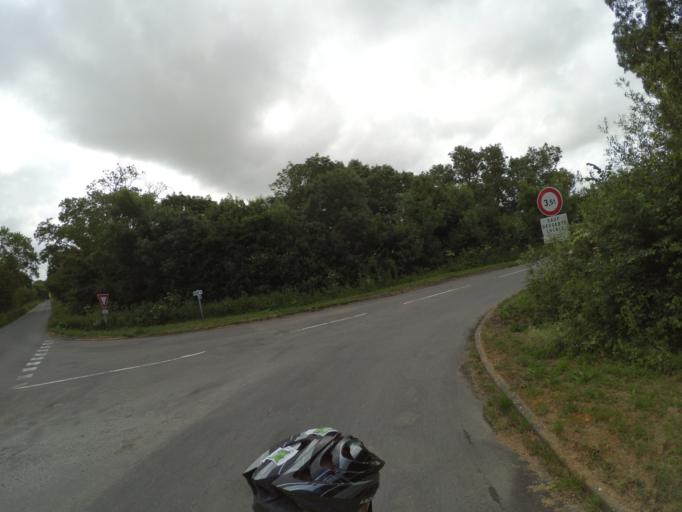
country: FR
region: Poitou-Charentes
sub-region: Departement de la Charente-Maritime
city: Yves
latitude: 46.0427
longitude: -1.0397
